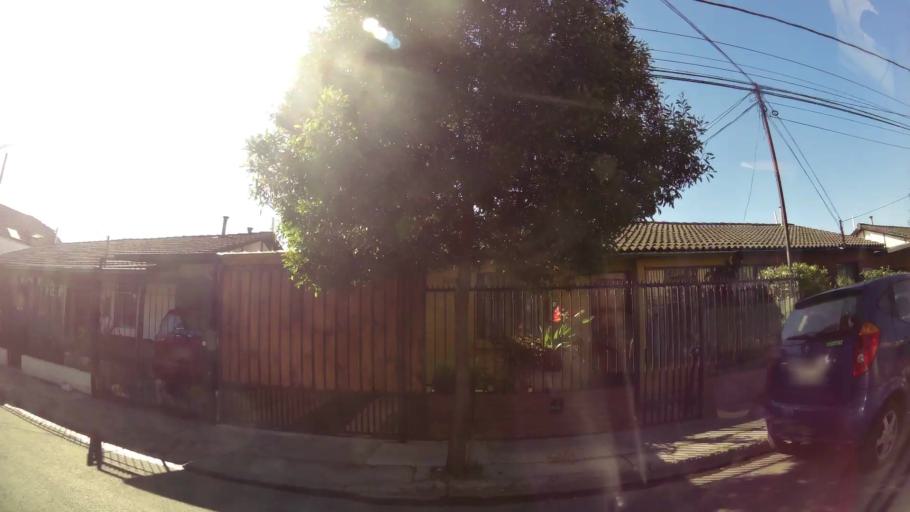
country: CL
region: Santiago Metropolitan
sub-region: Provincia de Maipo
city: San Bernardo
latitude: -33.5610
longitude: -70.7888
